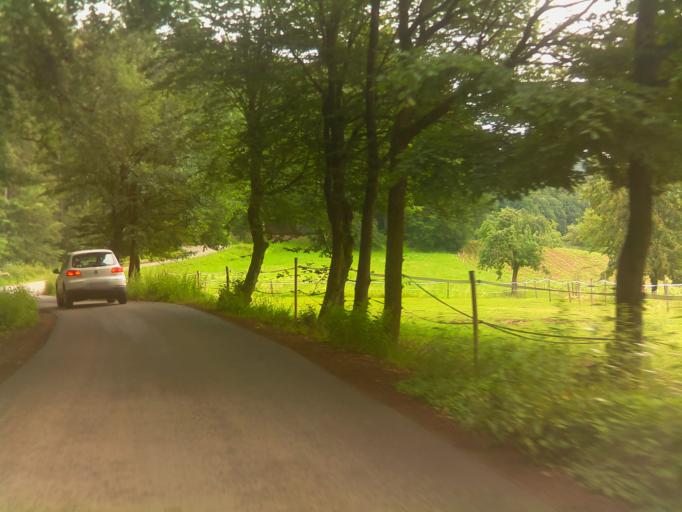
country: DE
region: Bavaria
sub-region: Regierungsbezirk Unterfranken
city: Johannesberg
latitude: 50.0704
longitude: 9.1133
